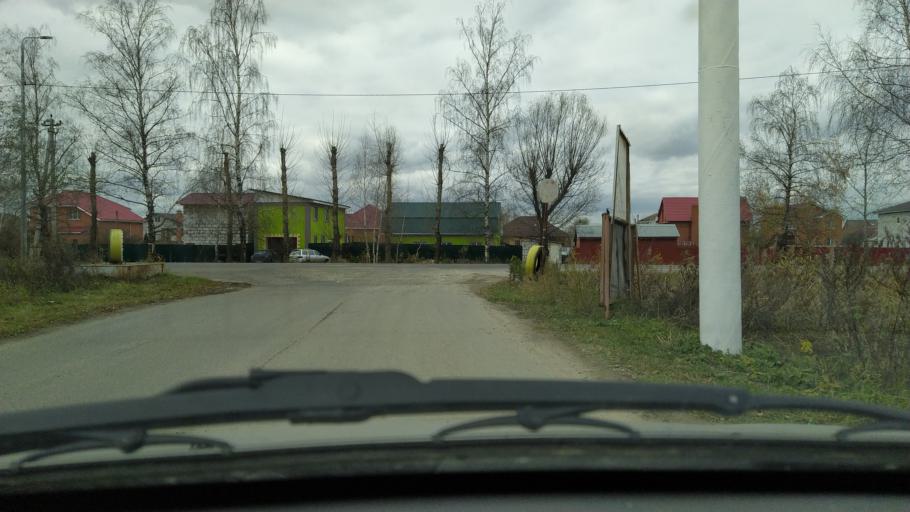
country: RU
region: Moskovskaya
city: Lopatinskiy
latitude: 55.3321
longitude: 38.7255
